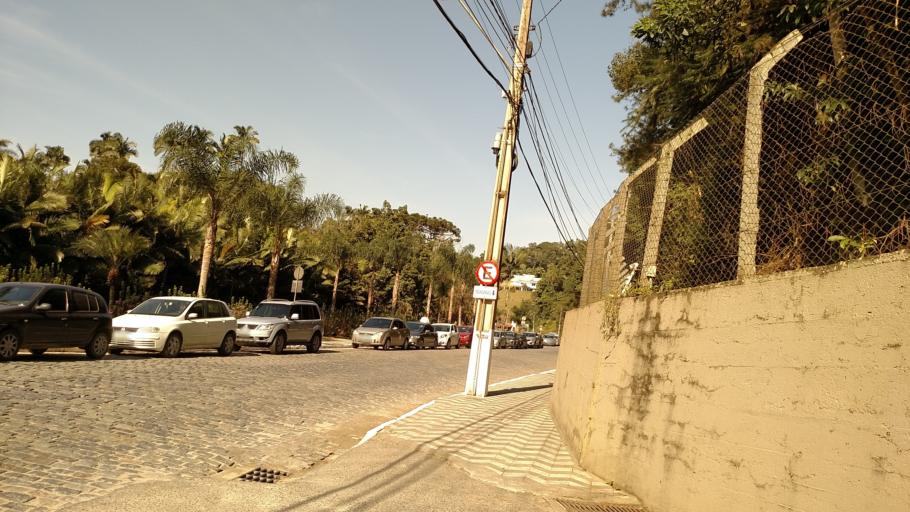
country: BR
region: Santa Catarina
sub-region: Pomerode
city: Pomerode
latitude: -26.7290
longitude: -49.0677
